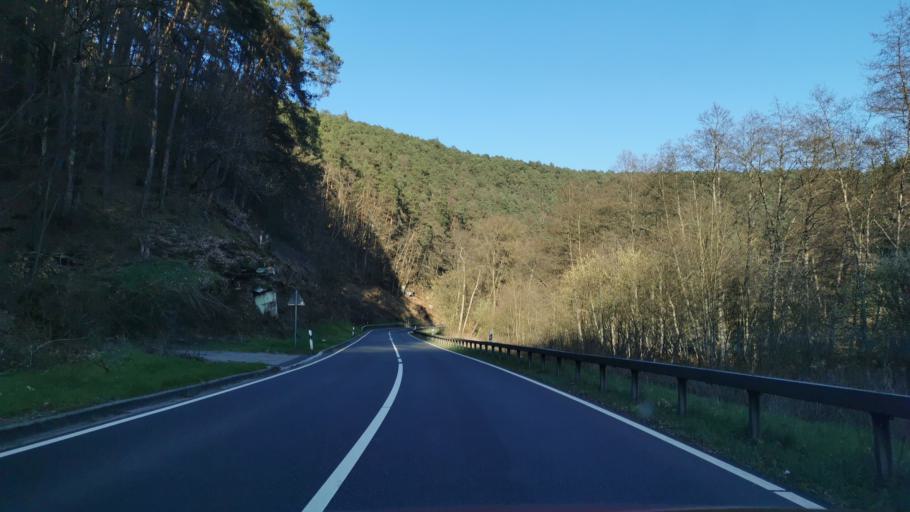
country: DE
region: Rheinland-Pfalz
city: Kordel
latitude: 49.8200
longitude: 6.6649
